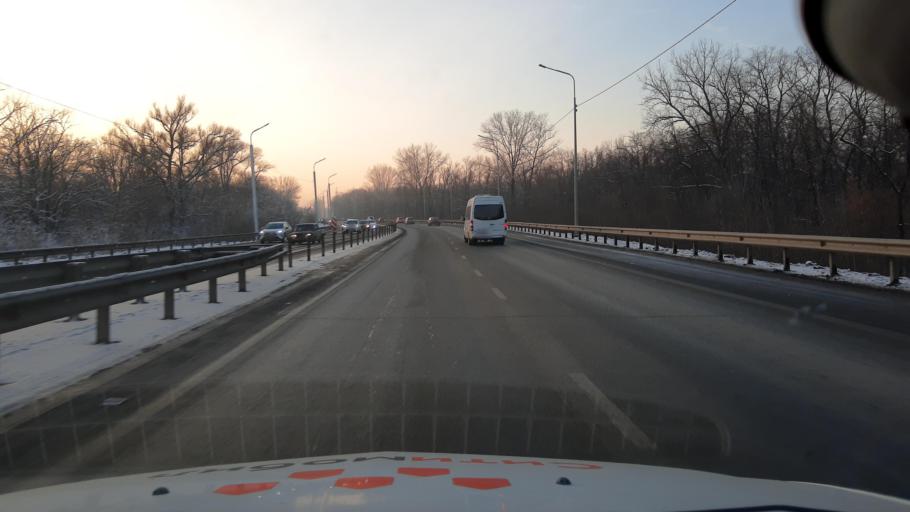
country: RU
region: Bashkortostan
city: Ufa
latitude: 54.7013
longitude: 55.9121
